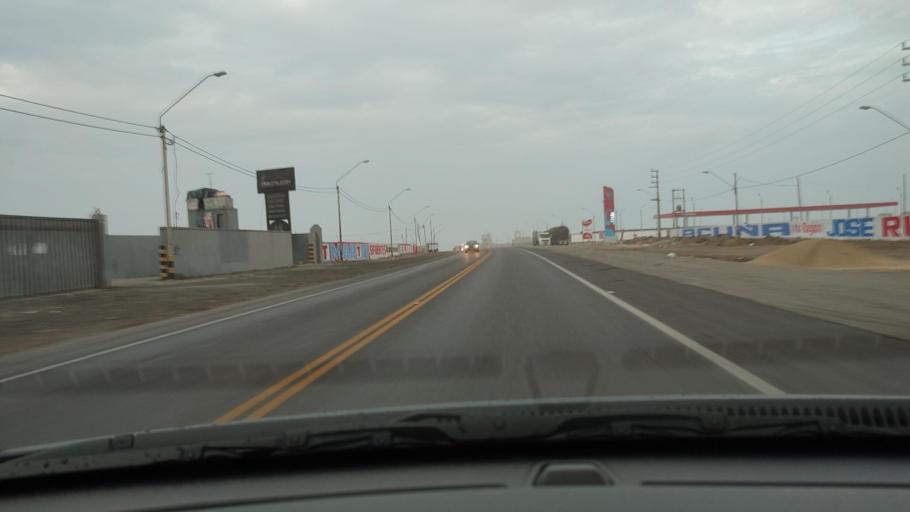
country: PE
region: La Libertad
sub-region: Provincia de Trujillo
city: Huanchaco
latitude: -8.1008
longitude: -79.0991
